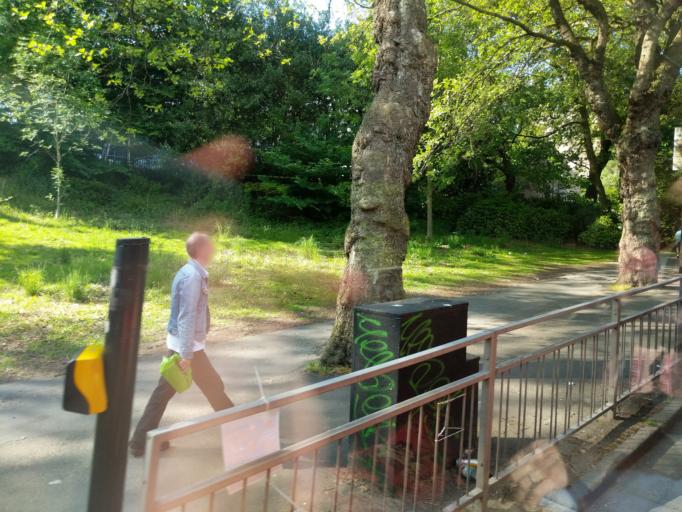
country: GB
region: Scotland
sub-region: Glasgow City
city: Glasgow
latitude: 55.8715
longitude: -4.2854
